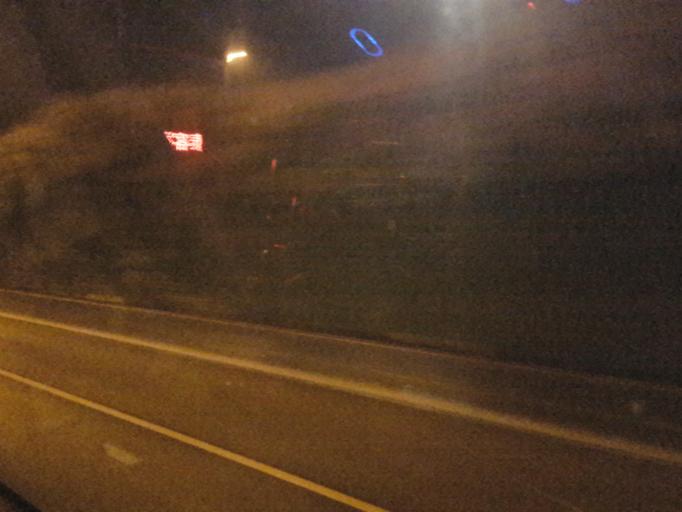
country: TW
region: Taiwan
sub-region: Hsinchu
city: Zhubei
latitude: 24.8706
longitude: 121.0177
